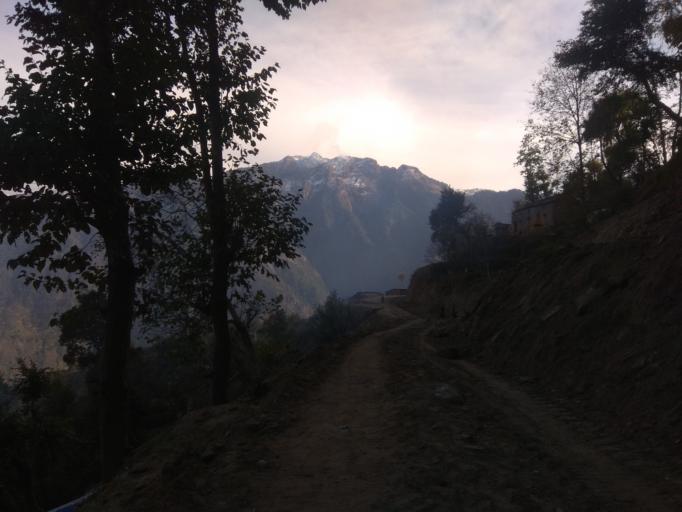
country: NP
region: Mid Western
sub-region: Bheri Zone
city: Dailekh
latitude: 29.2512
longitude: 81.6602
